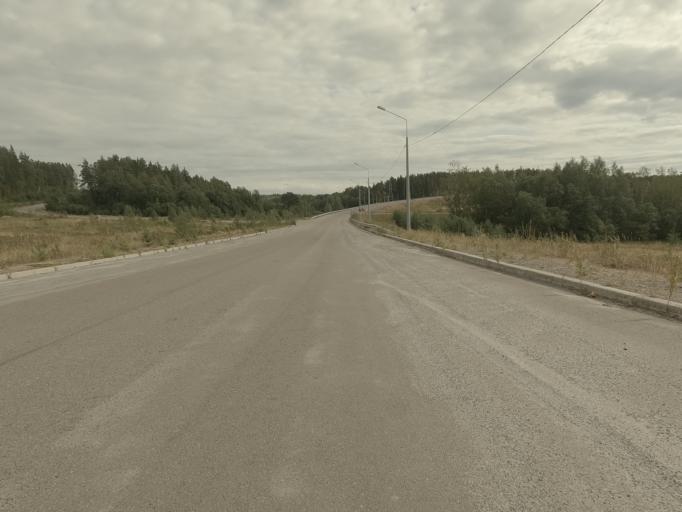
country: RU
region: Leningrad
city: Kamennogorsk
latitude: 60.9663
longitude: 29.1397
